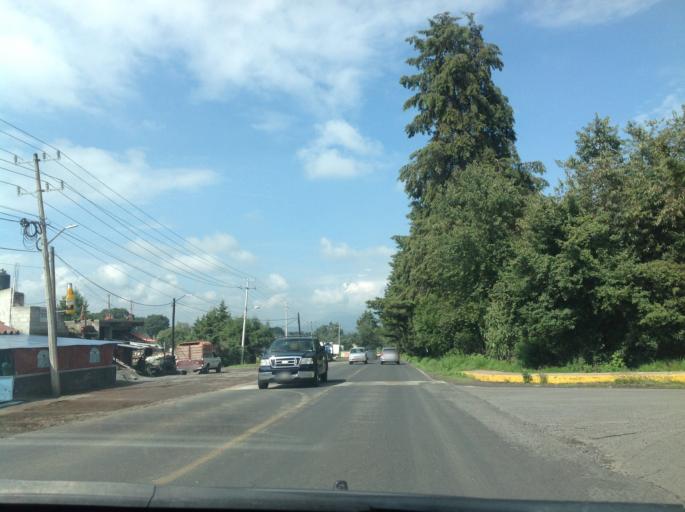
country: MX
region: Mexico
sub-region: Xalatlaco
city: Mezapa la Fabrica
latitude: 19.1788
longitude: -99.4438
